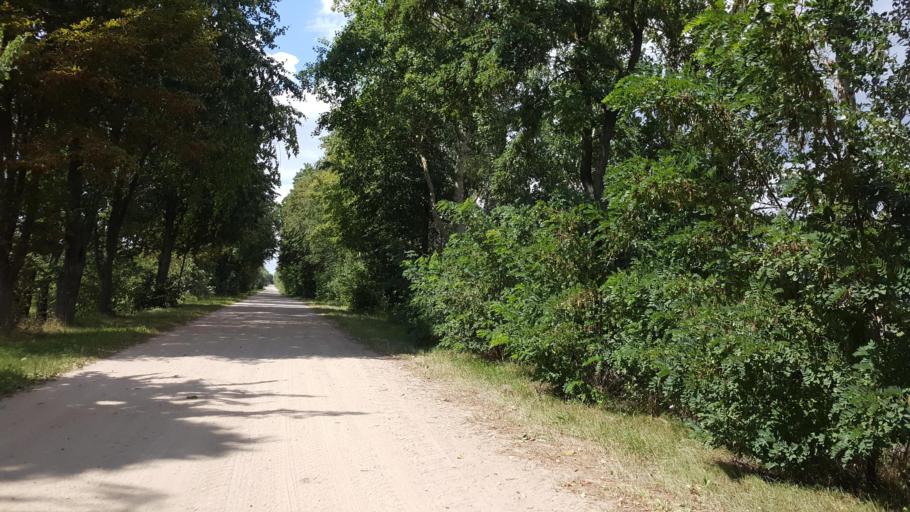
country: BY
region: Brest
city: Zhabinka
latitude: 52.2637
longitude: 24.0153
